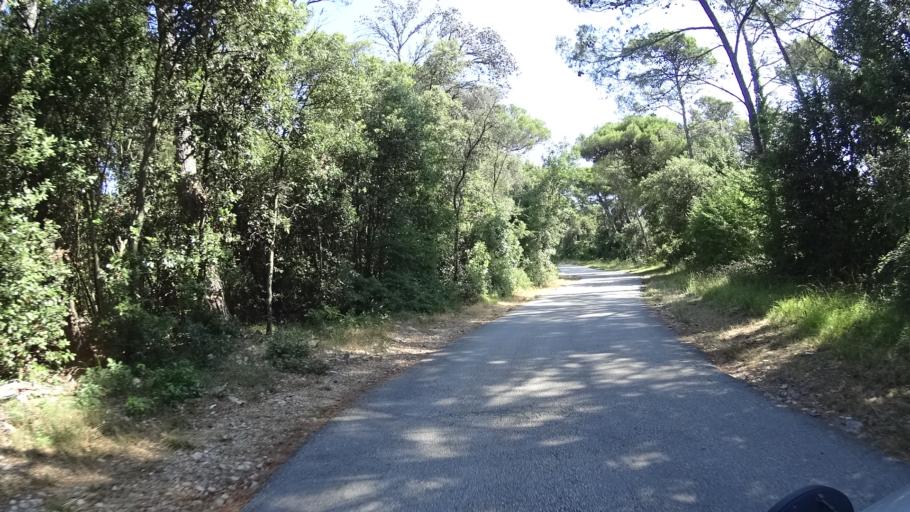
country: HR
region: Istarska
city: Rasa
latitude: 44.9746
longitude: 14.1044
